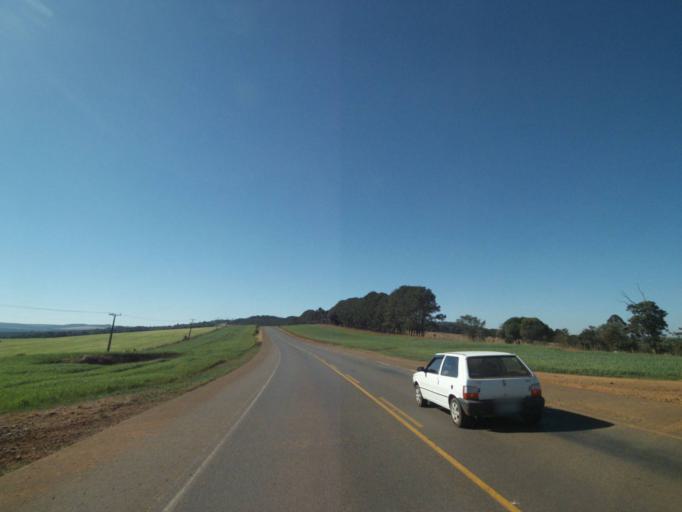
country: BR
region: Parana
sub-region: Tibagi
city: Tibagi
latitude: -24.4223
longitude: -50.3736
